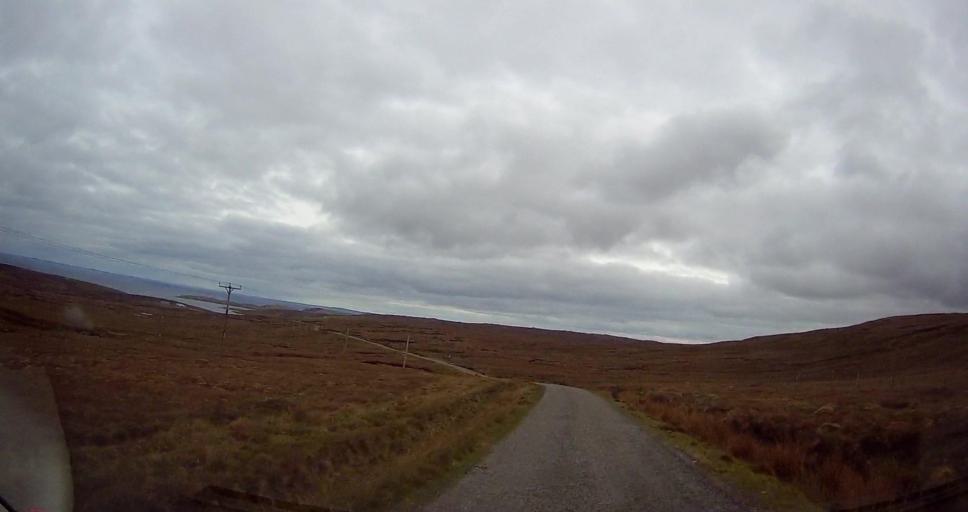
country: GB
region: Scotland
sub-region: Shetland Islands
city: Shetland
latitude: 60.5689
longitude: -1.0676
